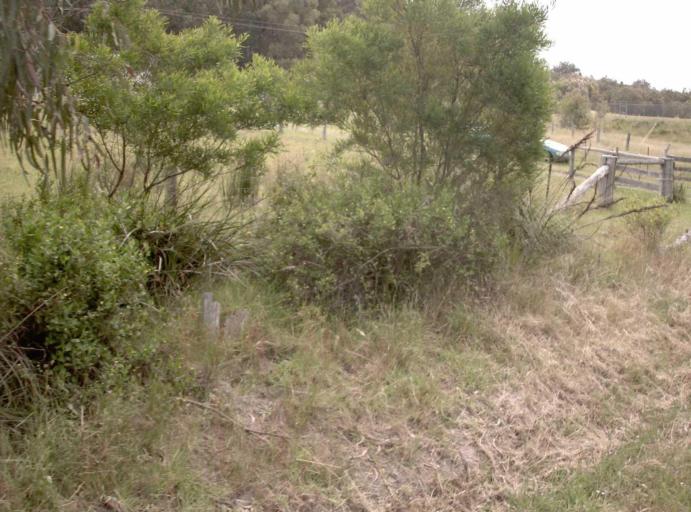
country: AU
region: Victoria
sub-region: Latrobe
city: Traralgon
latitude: -38.5022
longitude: 146.6480
